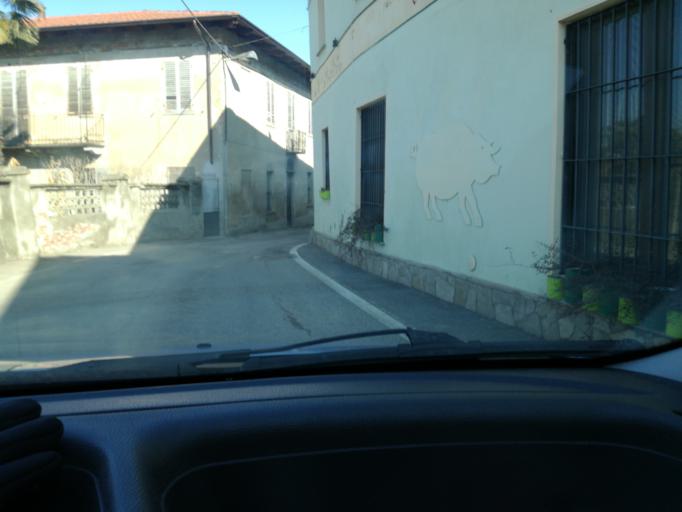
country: IT
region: Piedmont
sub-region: Provincia di Torino
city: Verrua Savoia
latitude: 45.1573
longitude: 8.0933
